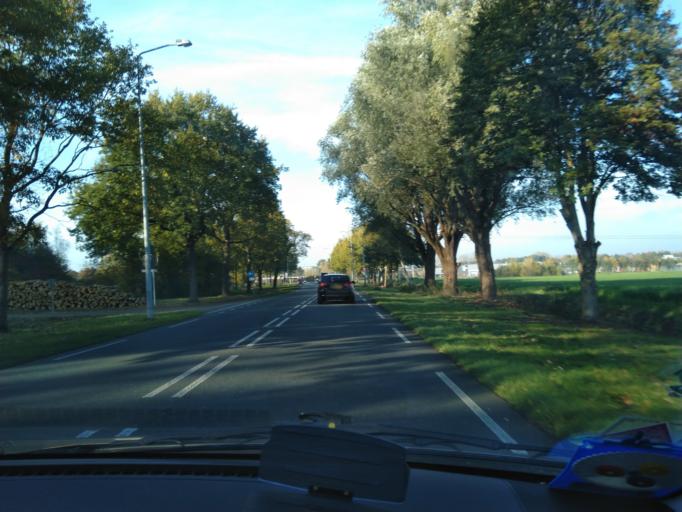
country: NL
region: Groningen
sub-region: Gemeente Hoogezand-Sappemeer
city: Hoogezand
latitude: 53.1463
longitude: 6.7653
